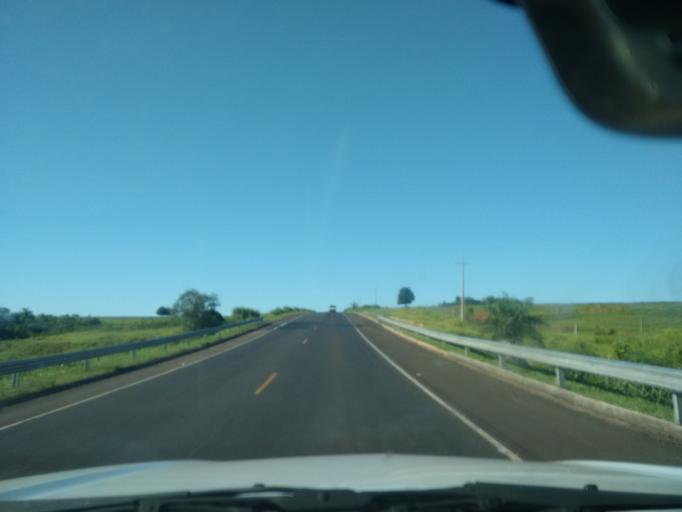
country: PY
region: Canindeyu
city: Salto del Guaira
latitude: -23.9803
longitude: -54.3310
